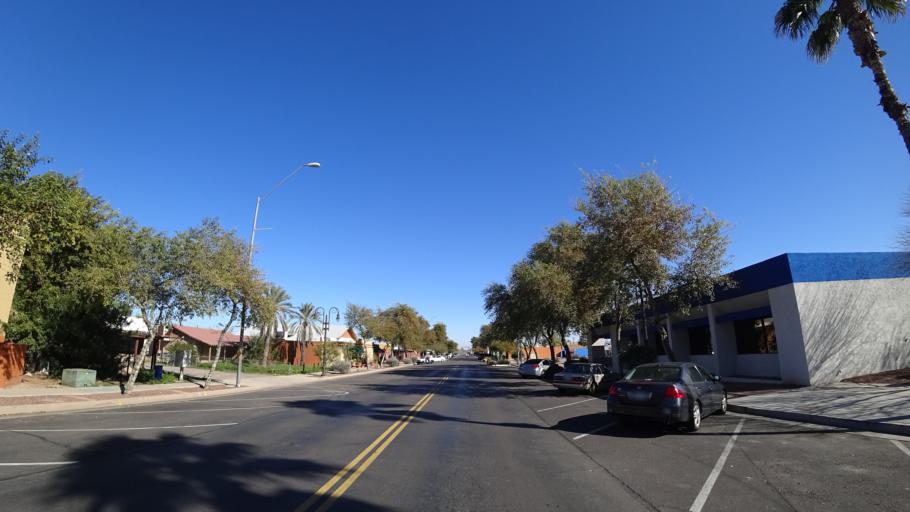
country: US
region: Arizona
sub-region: Maricopa County
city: Avondale
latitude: 33.4353
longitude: -112.3445
